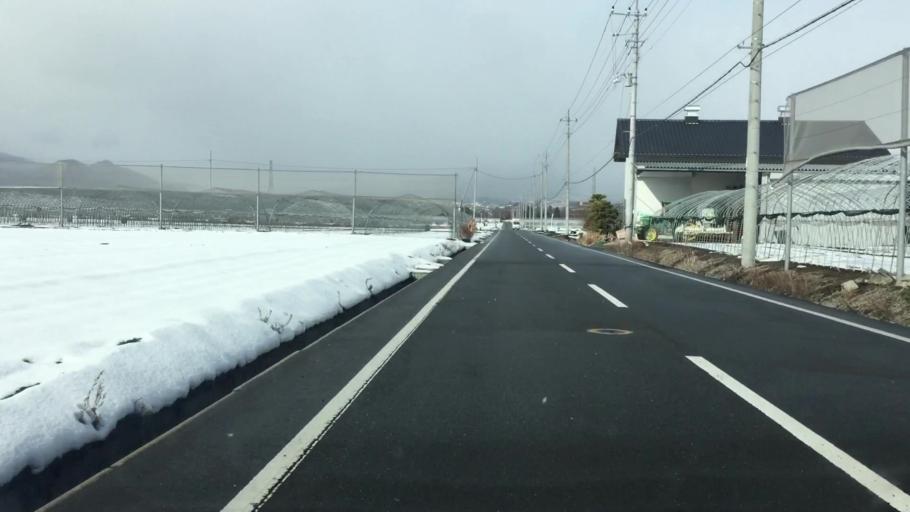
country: JP
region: Gunma
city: Numata
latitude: 36.6317
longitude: 139.0882
